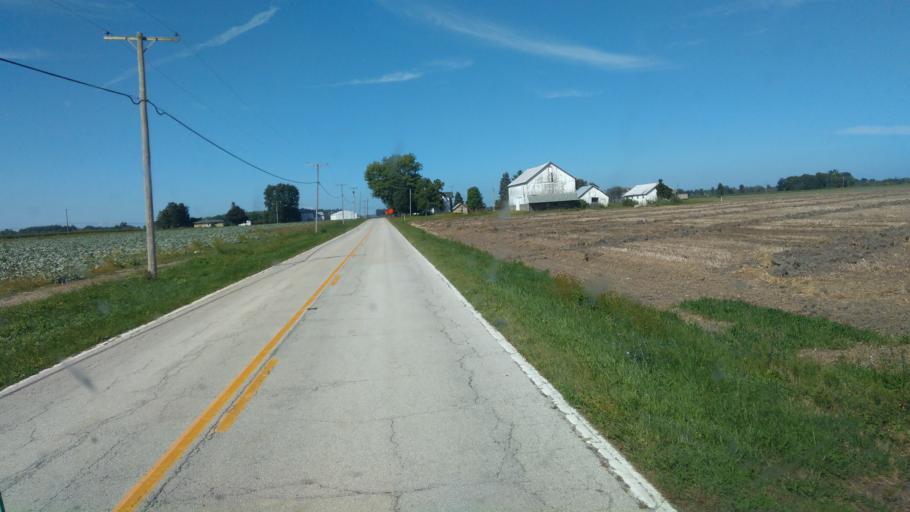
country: US
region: Ohio
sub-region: Ottawa County
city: Port Clinton
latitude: 41.4124
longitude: -82.8943
